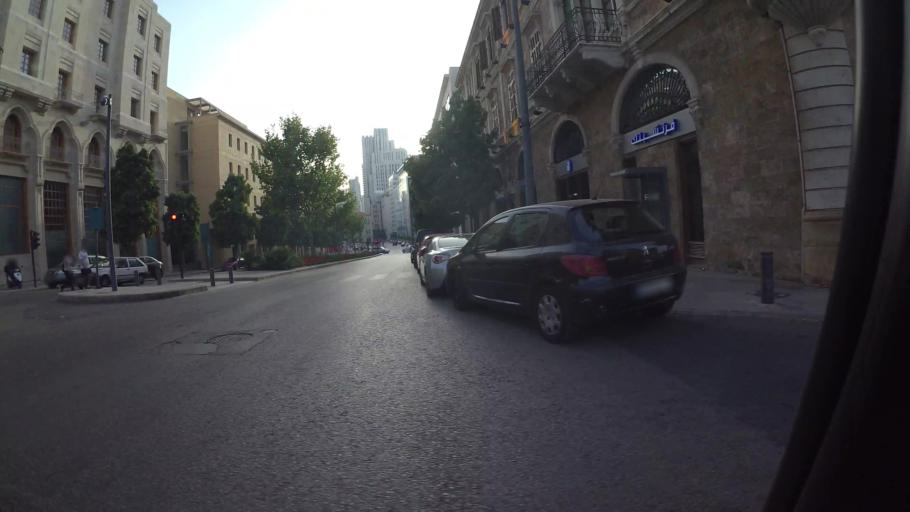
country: LB
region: Beyrouth
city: Beirut
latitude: 33.8987
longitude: 35.5025
